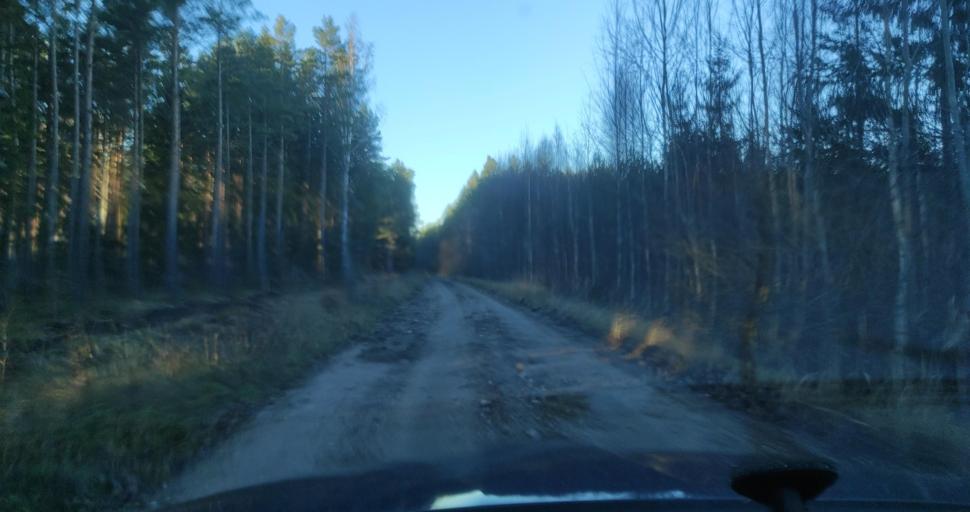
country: LV
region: Dundaga
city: Dundaga
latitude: 57.3813
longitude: 22.0814
